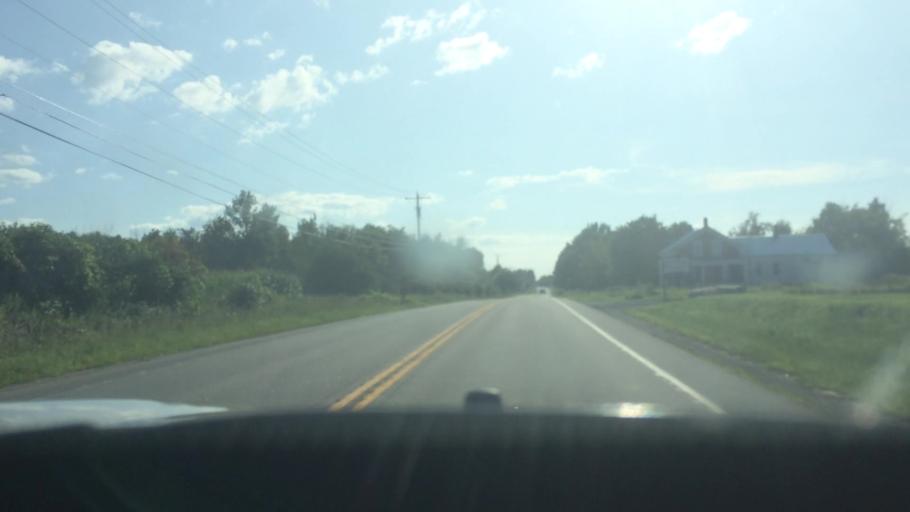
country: US
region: New York
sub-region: Franklin County
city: Malone
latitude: 44.8007
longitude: -74.4477
